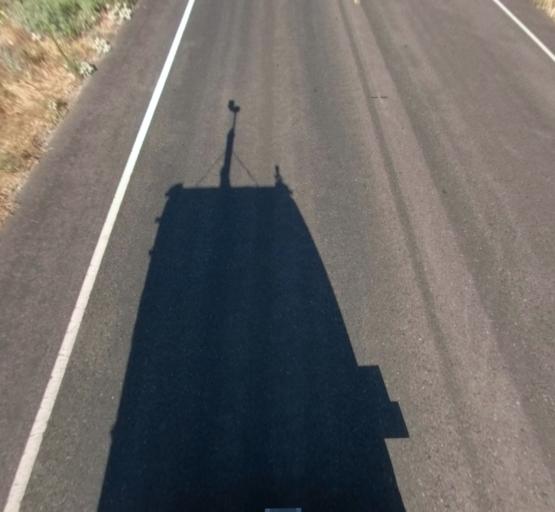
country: US
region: California
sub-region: Madera County
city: Parksdale
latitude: 36.9666
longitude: -119.9679
